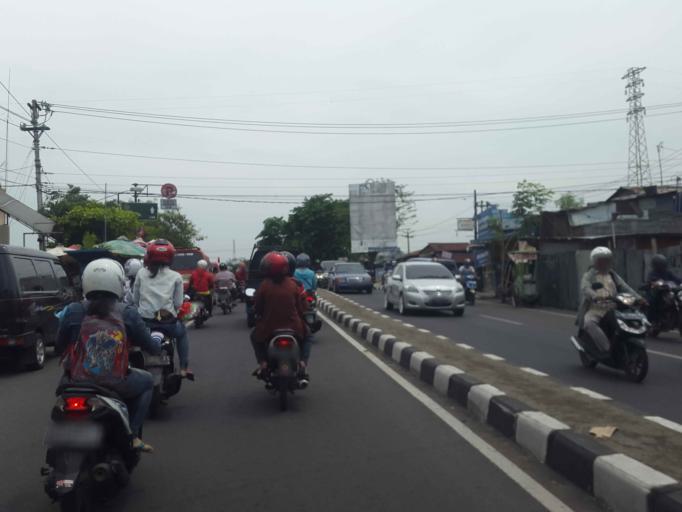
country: ID
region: Central Java
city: Semarang
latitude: -7.0105
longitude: 110.4409
